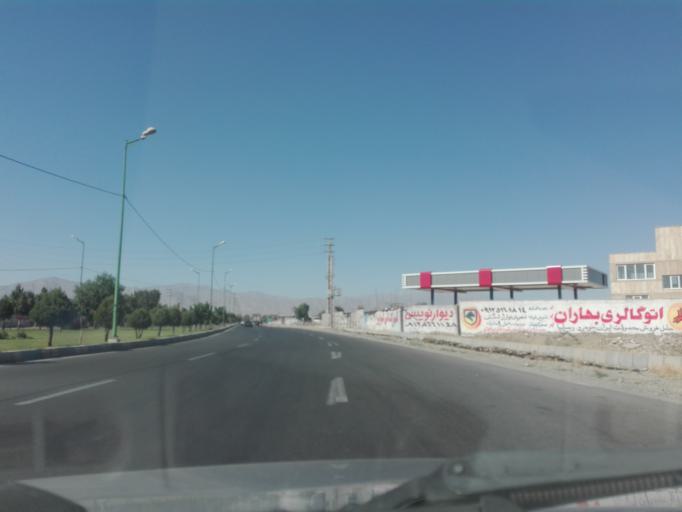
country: IR
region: Tehran
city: Shahriar
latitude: 35.6264
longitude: 51.0536
